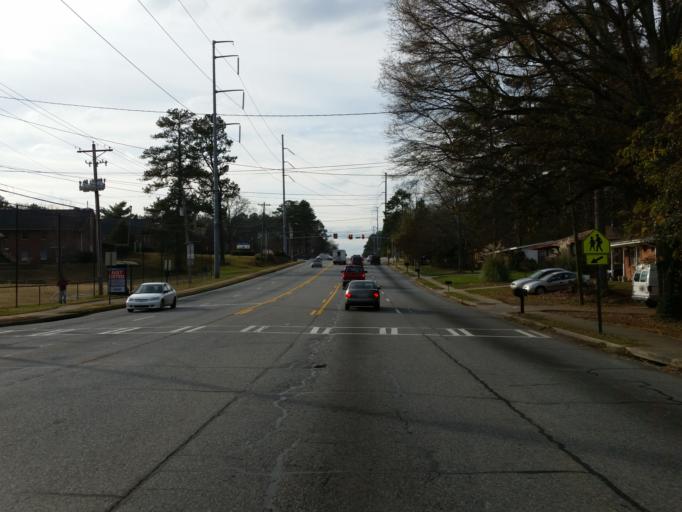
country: US
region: Georgia
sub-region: Cobb County
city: Fair Oaks
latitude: 33.8949
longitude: -84.5643
